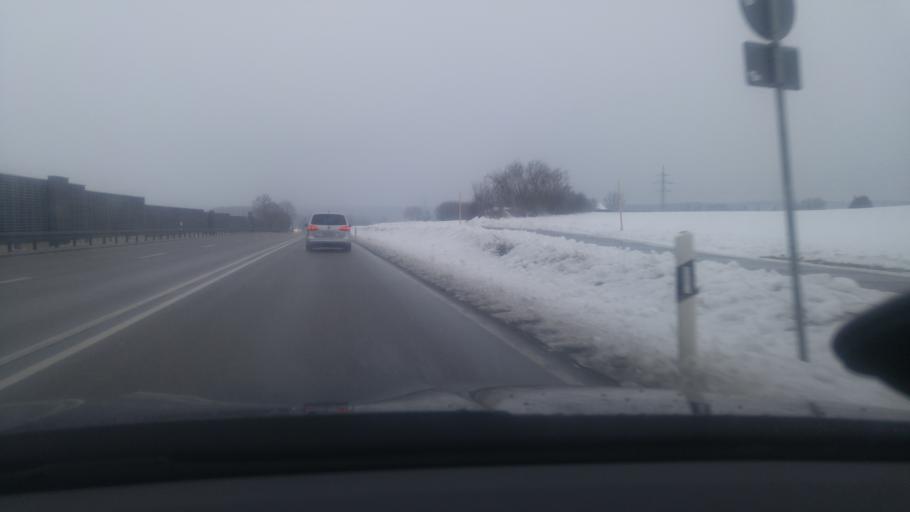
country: DE
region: Baden-Wuerttemberg
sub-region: Freiburg Region
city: Loffingen
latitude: 47.8898
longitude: 8.3458
